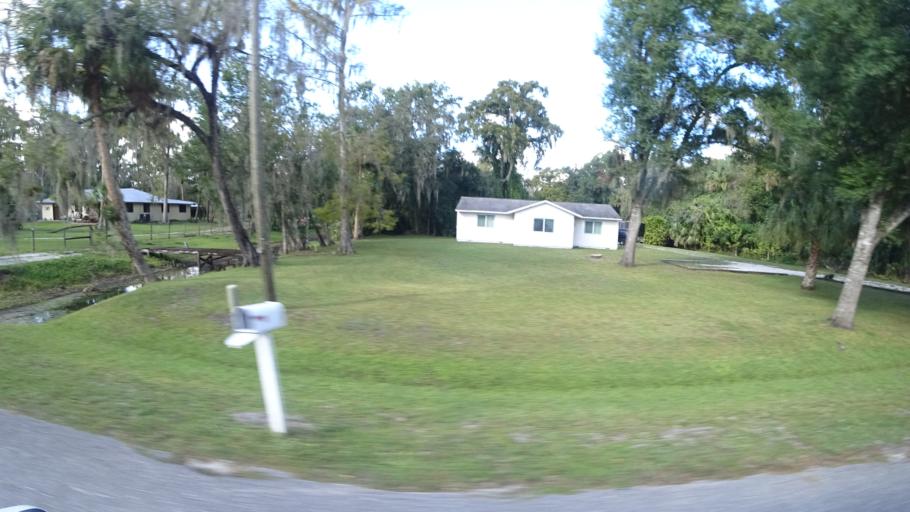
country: US
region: Florida
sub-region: Manatee County
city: Ellenton
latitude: 27.4829
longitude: -82.4730
